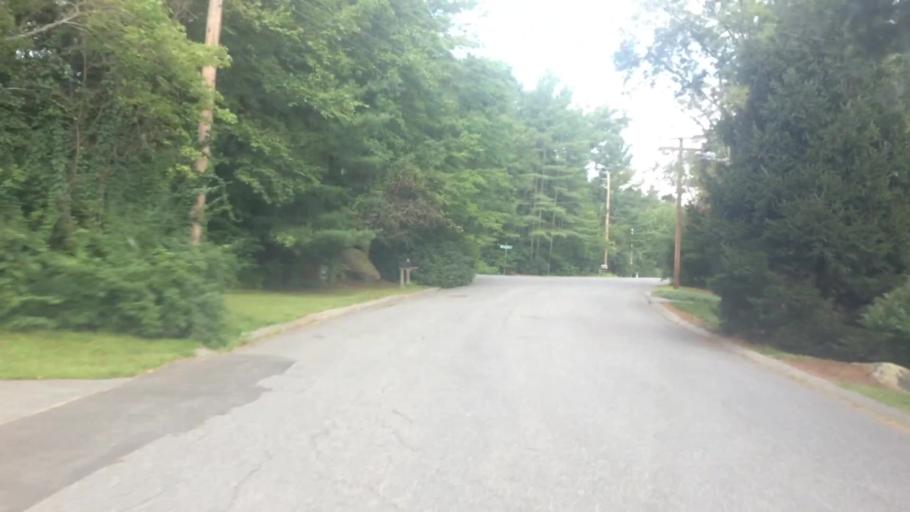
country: US
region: Massachusetts
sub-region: Middlesex County
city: Acton
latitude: 42.4608
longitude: -71.4364
